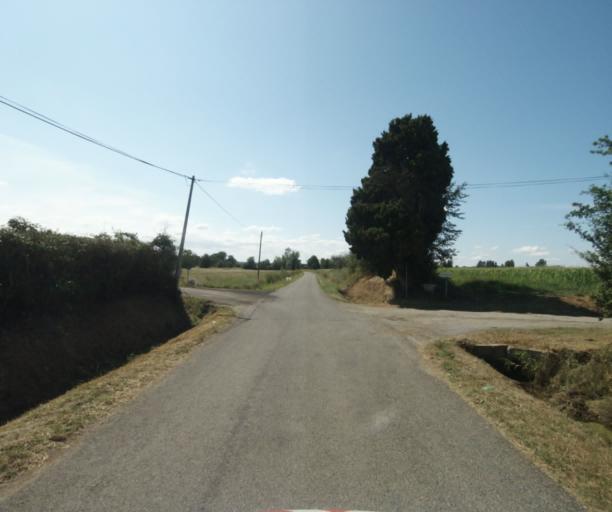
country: FR
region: Midi-Pyrenees
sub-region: Departement de la Haute-Garonne
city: Revel
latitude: 43.4739
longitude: 1.9850
